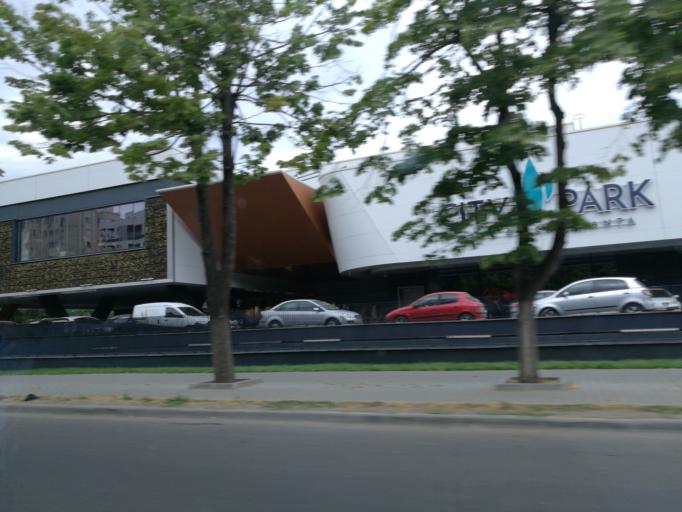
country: RO
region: Constanta
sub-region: Municipiul Constanta
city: Constanta
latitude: 44.2040
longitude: 28.6300
